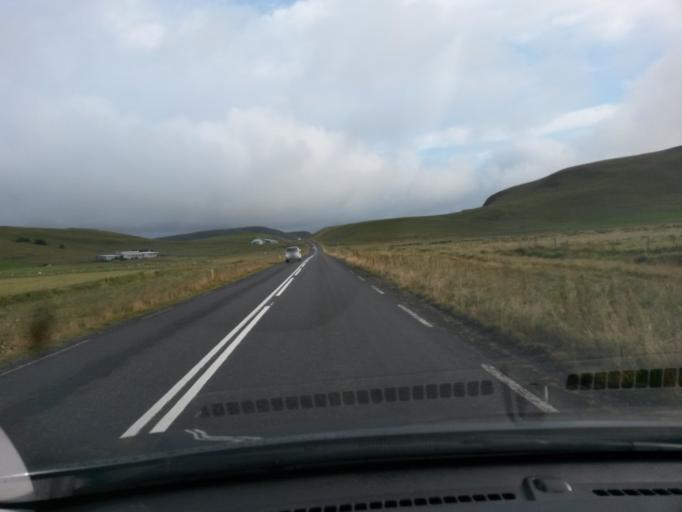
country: IS
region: South
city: Vestmannaeyjar
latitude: 63.4336
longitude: -19.1687
